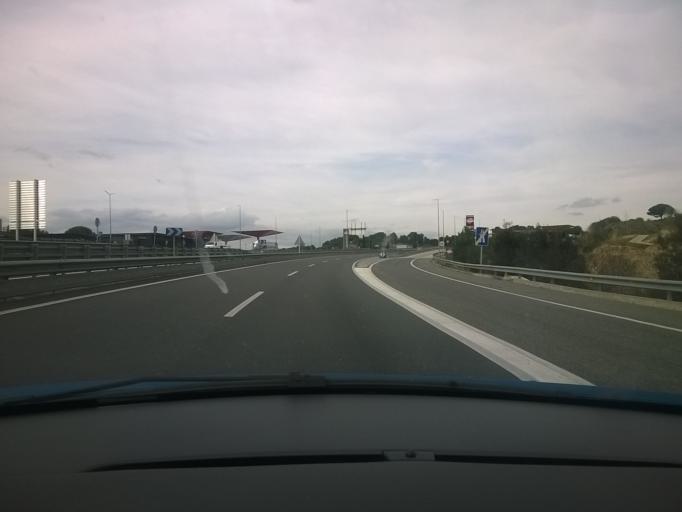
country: ES
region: Catalonia
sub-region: Provincia de Barcelona
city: Rubi
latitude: 41.4966
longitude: 2.0490
